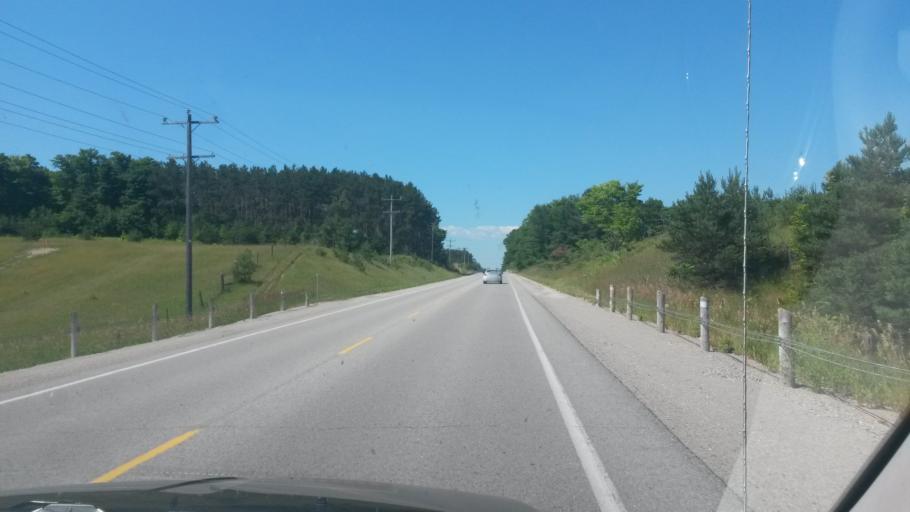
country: CA
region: Ontario
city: Barrie
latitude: 44.5377
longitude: -79.7081
